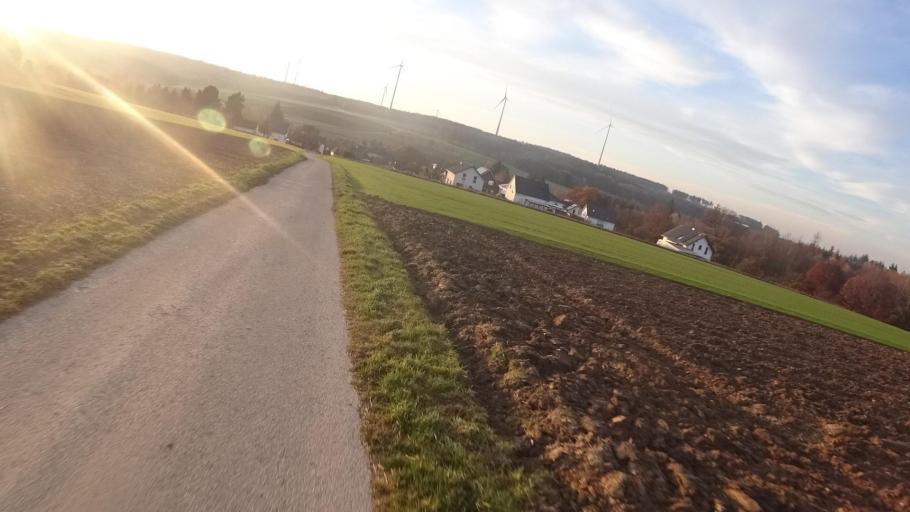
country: DE
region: Rheinland-Pfalz
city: Hausbay
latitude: 50.1075
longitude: 7.5658
